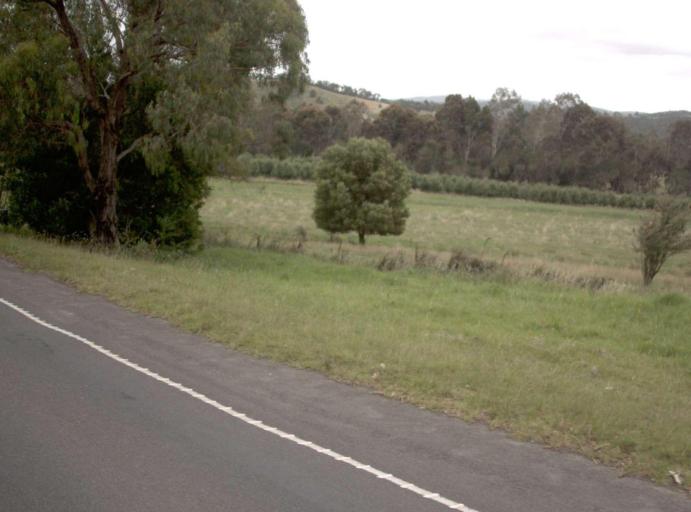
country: AU
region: Victoria
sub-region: Yarra Ranges
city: Yarra Glen
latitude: -37.5864
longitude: 145.4117
